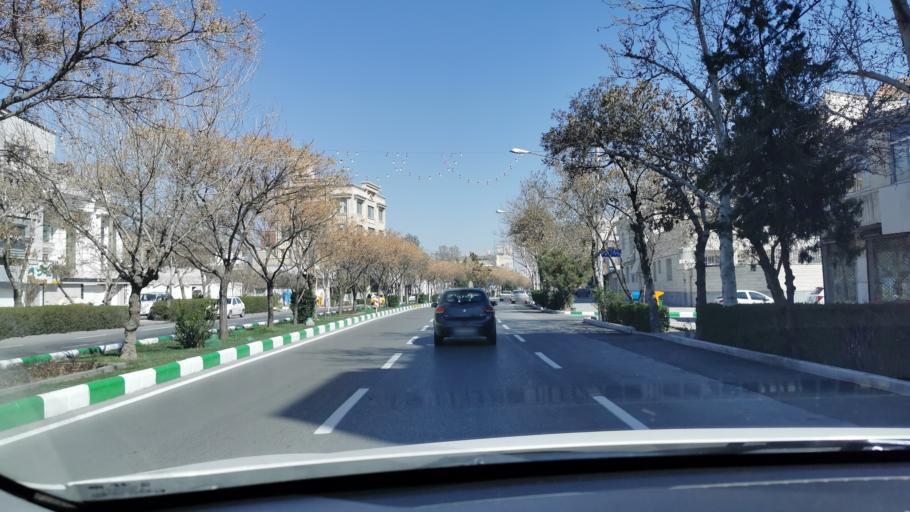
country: IR
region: Razavi Khorasan
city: Mashhad
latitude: 36.2932
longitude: 59.5723
